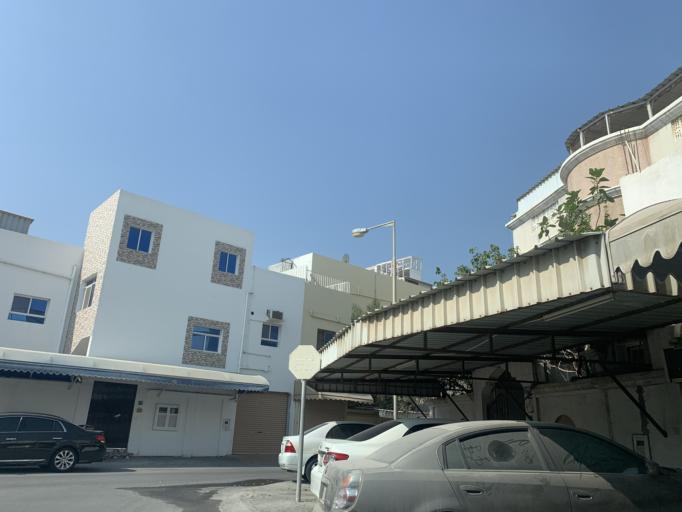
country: BH
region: Central Governorate
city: Madinat Hamad
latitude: 26.1267
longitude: 50.4937
